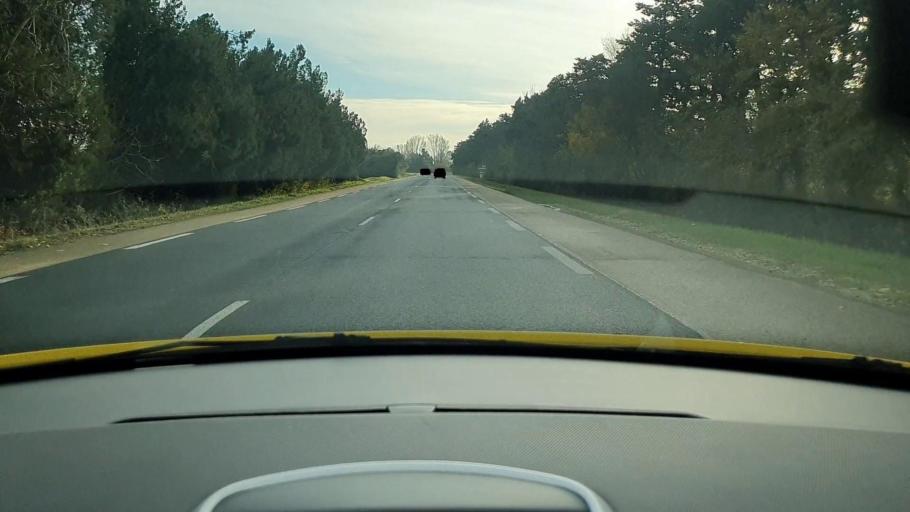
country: FR
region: Languedoc-Roussillon
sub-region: Departement du Gard
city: Fourques
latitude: 43.7014
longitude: 4.5731
